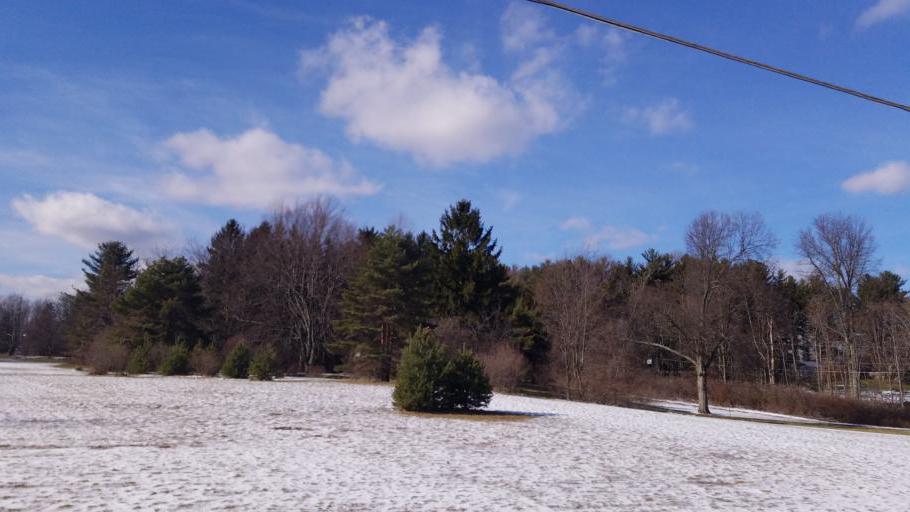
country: US
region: Ohio
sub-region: Richland County
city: Ontario
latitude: 40.7251
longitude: -82.5949
